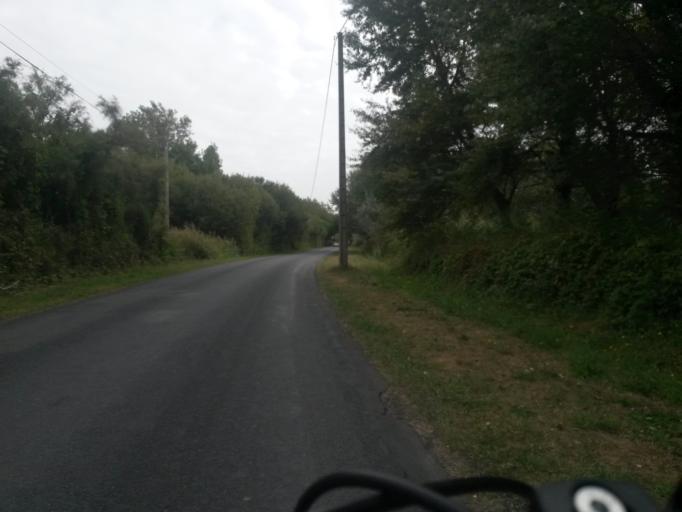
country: FR
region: Poitou-Charentes
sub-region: Departement de la Charente-Maritime
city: Saint-Denis-d'Oleron
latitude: 46.0086
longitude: -1.3867
